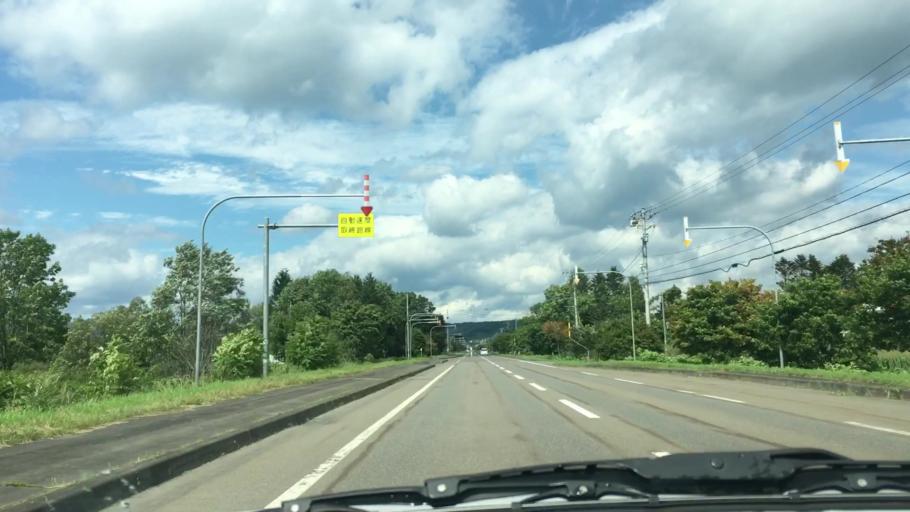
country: JP
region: Hokkaido
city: Otofuke
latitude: 43.2934
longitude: 143.3088
